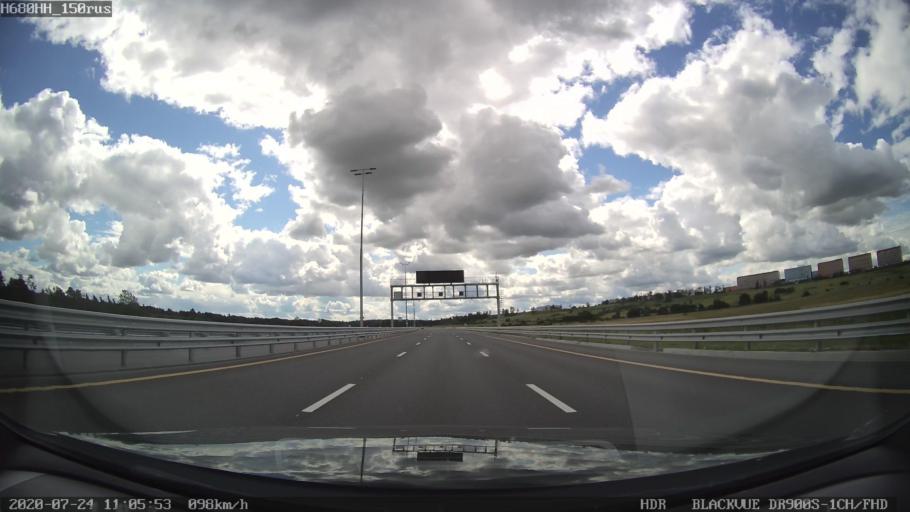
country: RU
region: St.-Petersburg
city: Shushary
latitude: 59.7710
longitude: 30.3635
